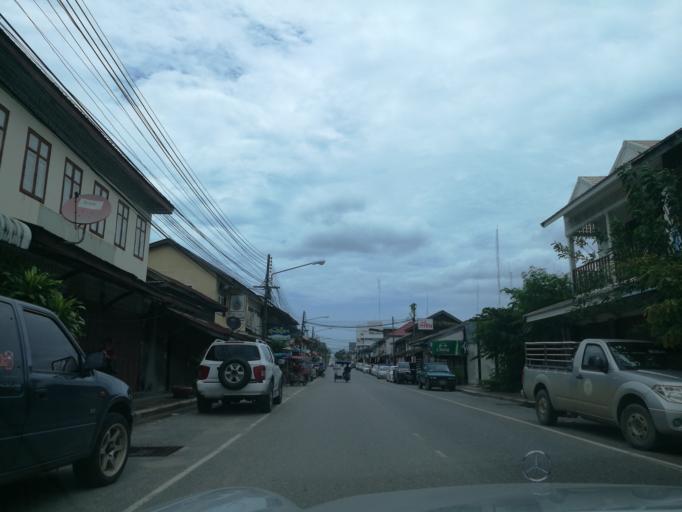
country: TH
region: Prachuap Khiri Khan
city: Prachuap Khiri Khan
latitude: 11.8080
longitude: 99.7944
